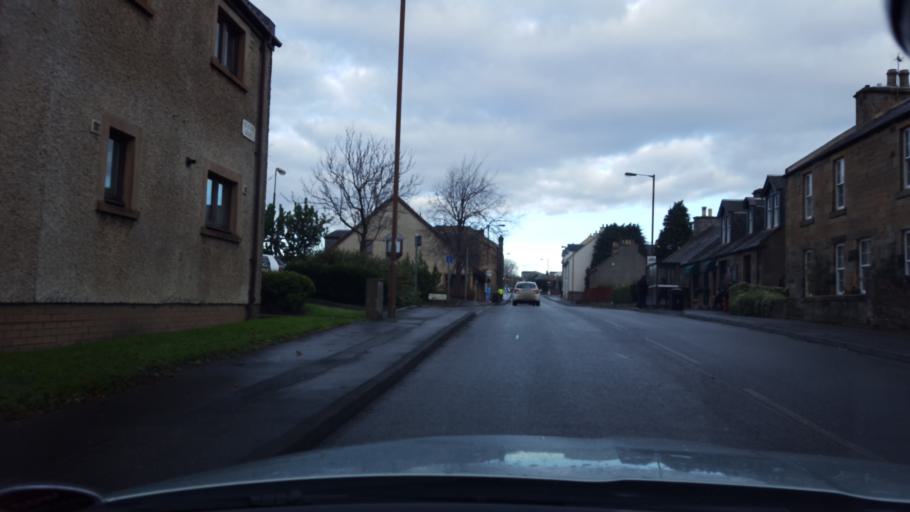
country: GB
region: Scotland
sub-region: Edinburgh
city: Kirkliston
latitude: 55.9547
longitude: -3.4010
